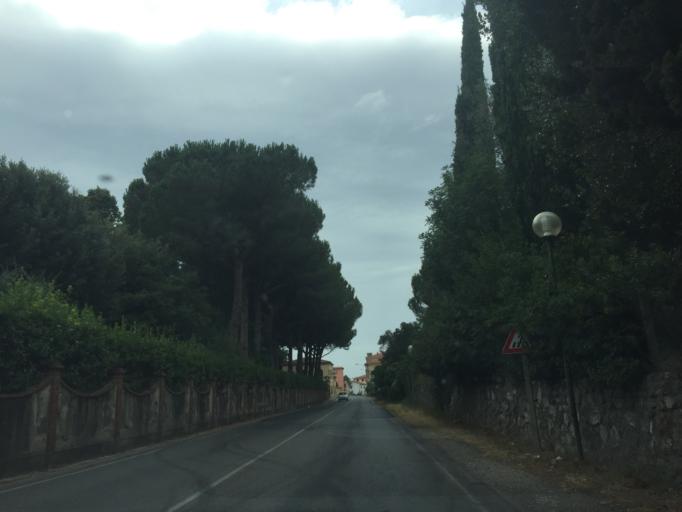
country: IT
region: Tuscany
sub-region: Province of Pisa
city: Uliveto Terme
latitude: 43.6922
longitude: 10.5252
